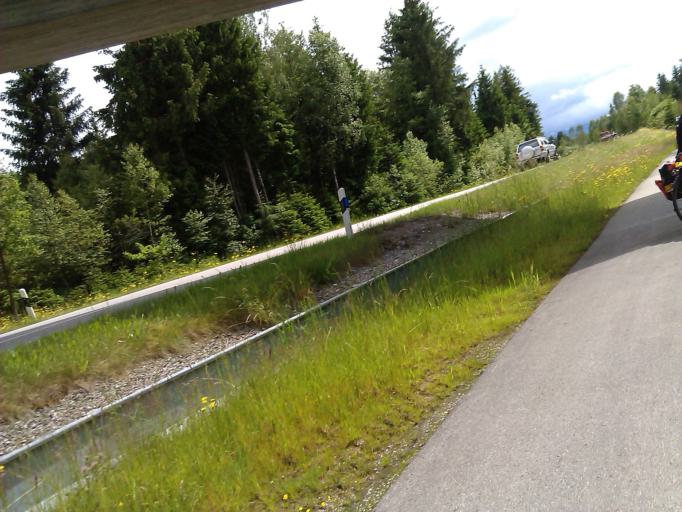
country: DE
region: Bavaria
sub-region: Swabia
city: Stotten am Auerberg
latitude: 47.7364
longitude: 10.6803
